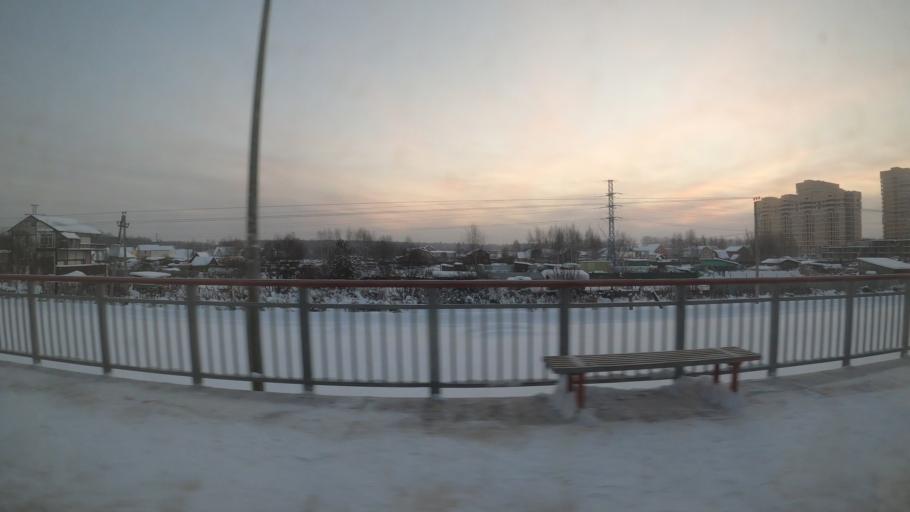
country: RU
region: Moskovskaya
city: Lobnya
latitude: 56.0282
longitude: 37.4869
